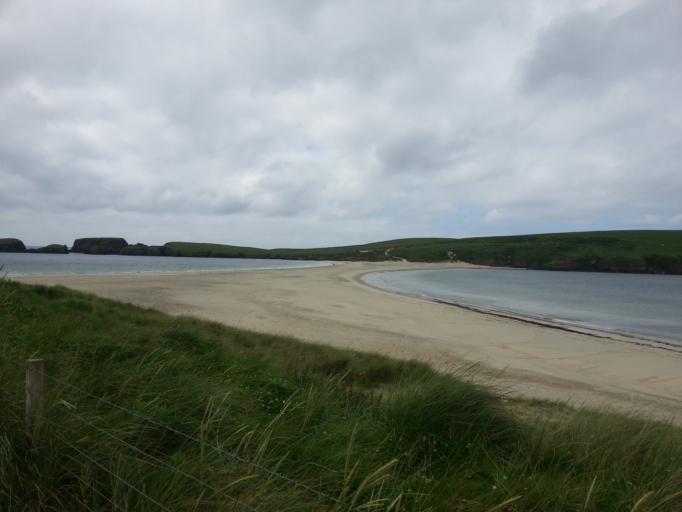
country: GB
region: Scotland
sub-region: Shetland Islands
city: Sandwick
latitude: 59.9708
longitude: -1.3311
